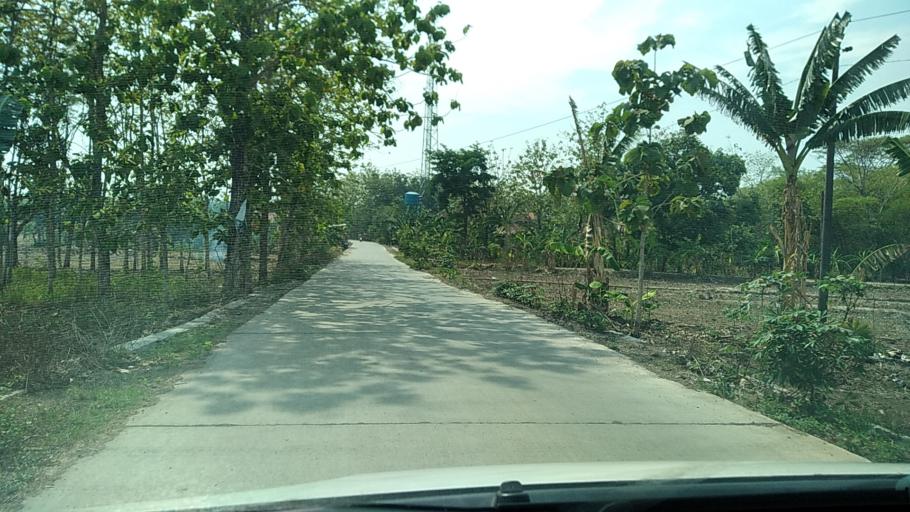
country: ID
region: Central Java
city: Mranggen
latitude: -7.0661
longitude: 110.4960
